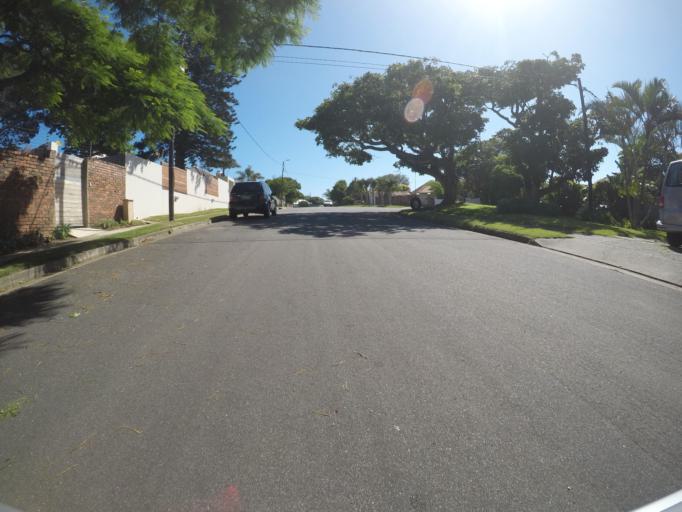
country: ZA
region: Eastern Cape
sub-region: Buffalo City Metropolitan Municipality
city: East London
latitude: -32.9850
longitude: 27.9437
